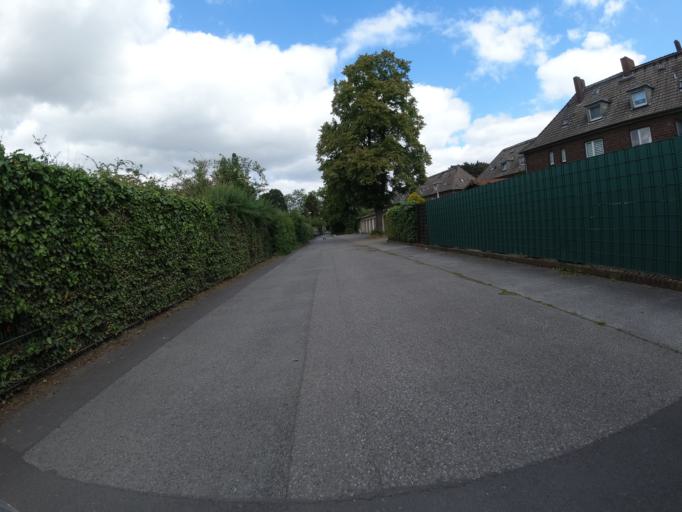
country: DE
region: North Rhine-Westphalia
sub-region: Regierungsbezirk Dusseldorf
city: Hochfeld
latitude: 51.3970
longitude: 6.6928
